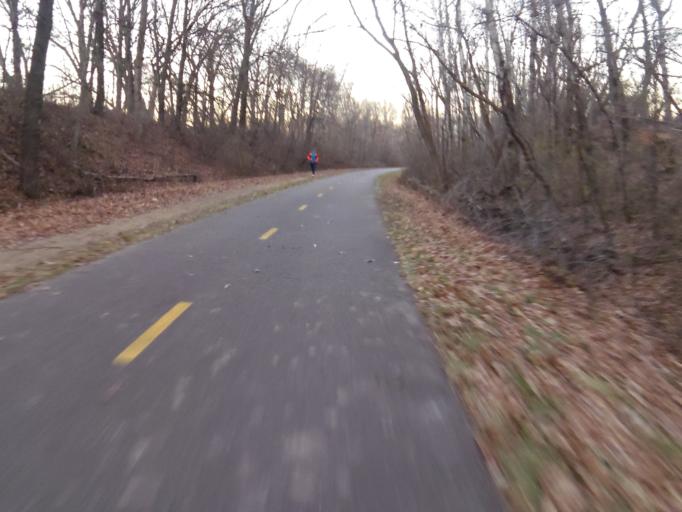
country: US
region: Minnesota
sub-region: Washington County
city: Grant
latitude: 45.0904
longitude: -92.8904
